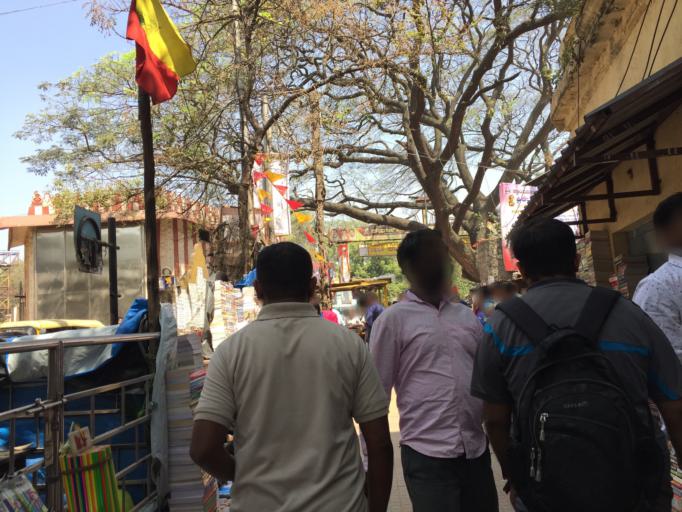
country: IN
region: Karnataka
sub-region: Bangalore Urban
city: Bangalore
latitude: 12.9723
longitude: 77.5810
